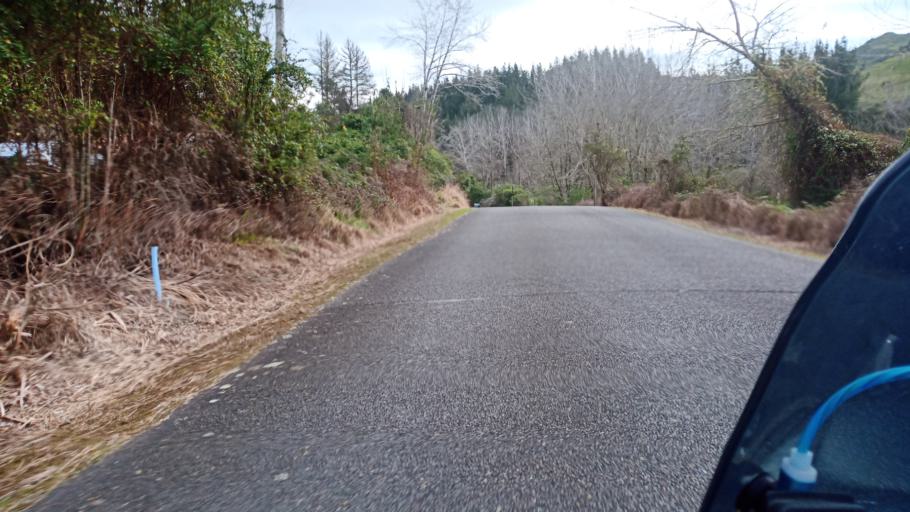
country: NZ
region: Hawke's Bay
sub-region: Wairoa District
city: Wairoa
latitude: -38.8257
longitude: 177.5118
